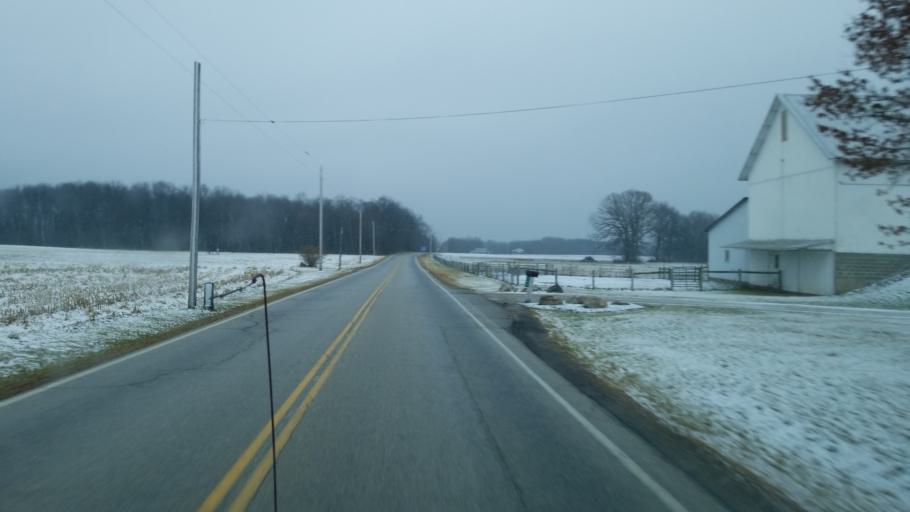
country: US
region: Ohio
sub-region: Ashland County
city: Loudonville
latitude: 40.7403
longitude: -82.1681
